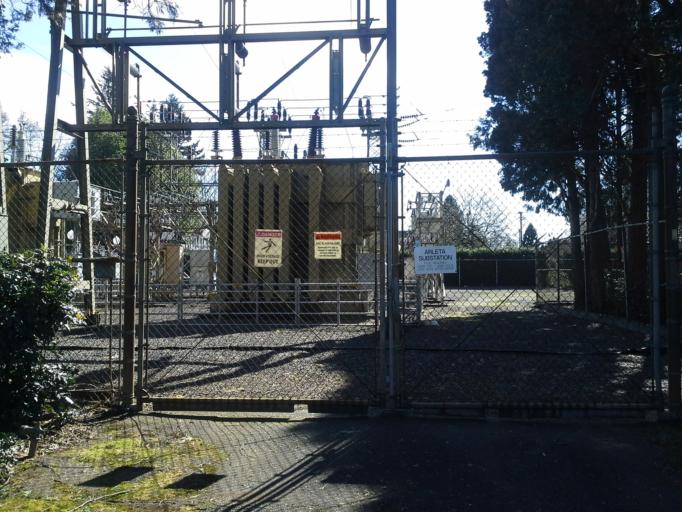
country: US
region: Oregon
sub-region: Multnomah County
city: Lents
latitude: 45.4890
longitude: -122.6078
